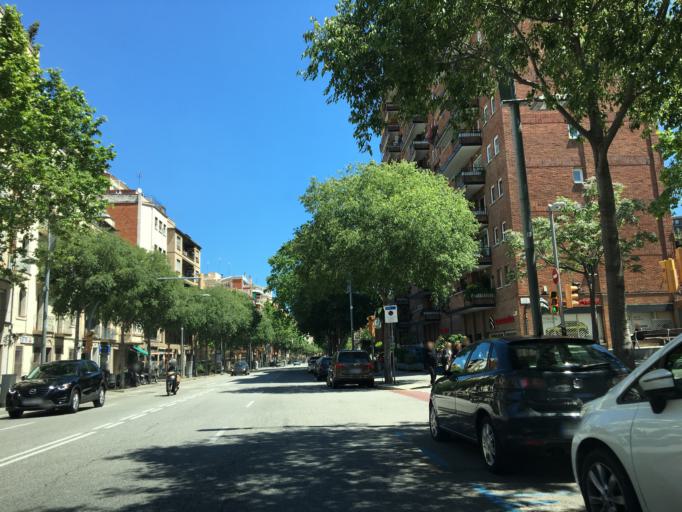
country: ES
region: Catalonia
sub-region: Provincia de Barcelona
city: Horta-Guinardo
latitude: 41.4277
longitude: 2.1658
